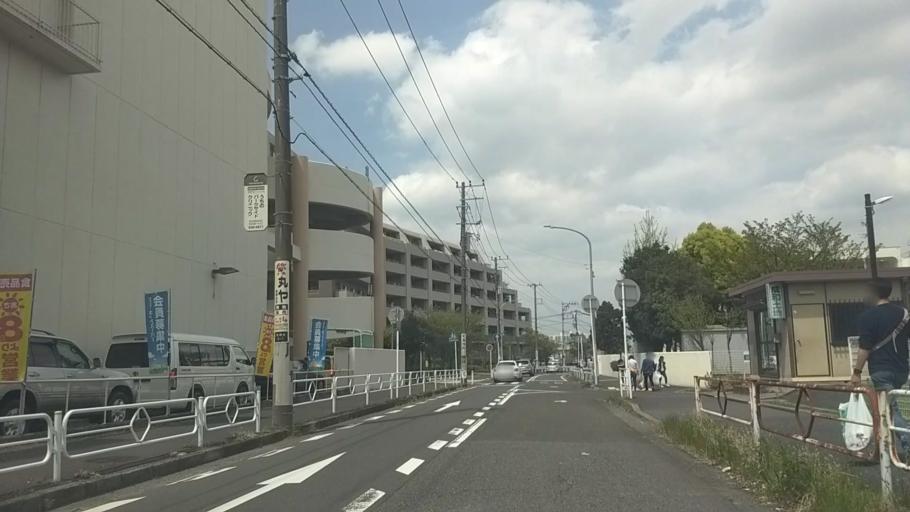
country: JP
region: Kanagawa
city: Kamakura
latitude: 35.3757
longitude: 139.5779
